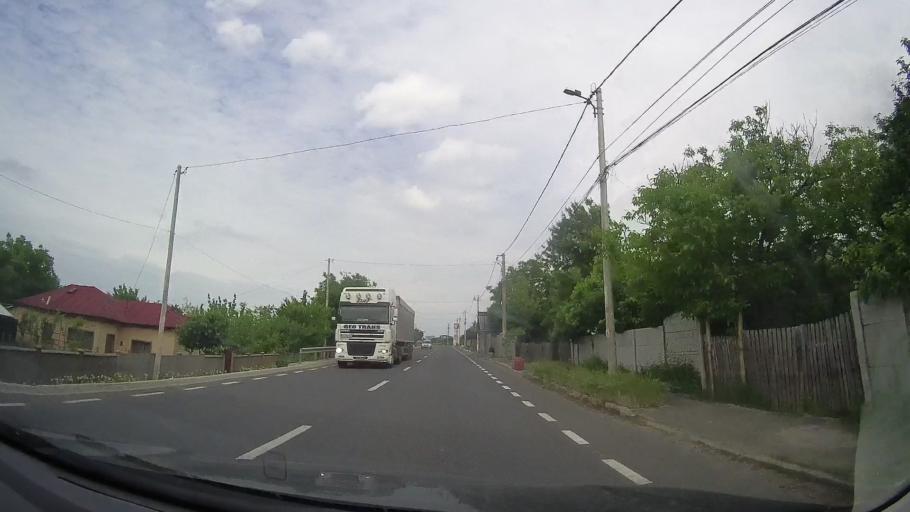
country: RO
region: Teleorman
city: Rosiori de Vede
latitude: 44.0973
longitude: 24.9918
